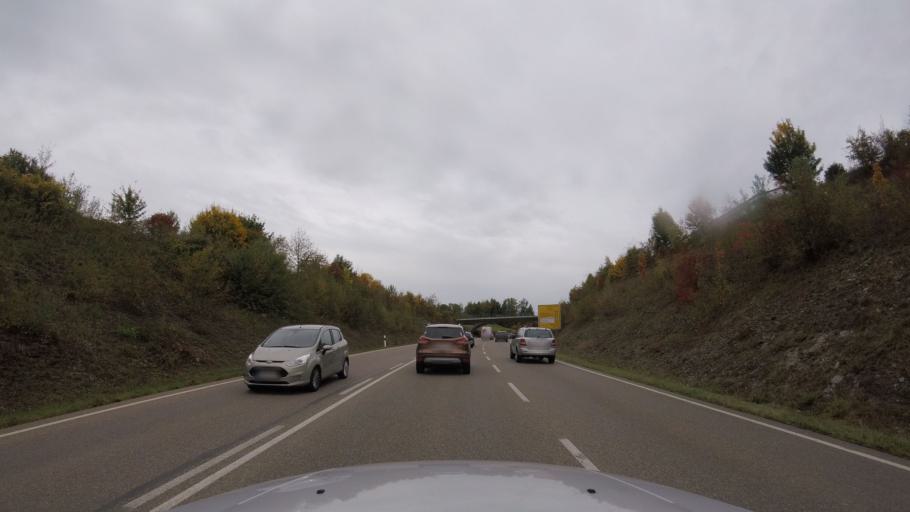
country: DE
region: Baden-Wuerttemberg
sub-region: Regierungsbezirk Stuttgart
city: Mutlangen
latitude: 48.8179
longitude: 9.7844
